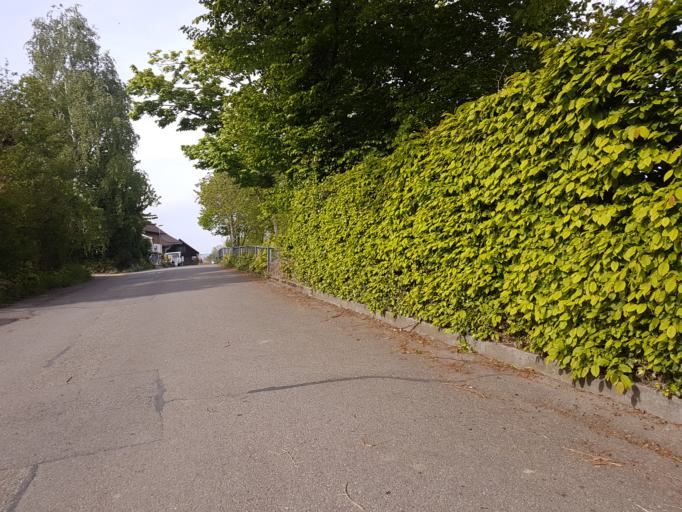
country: CH
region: Bern
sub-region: Seeland District
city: Tauffelen
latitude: 47.0978
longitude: 7.2105
